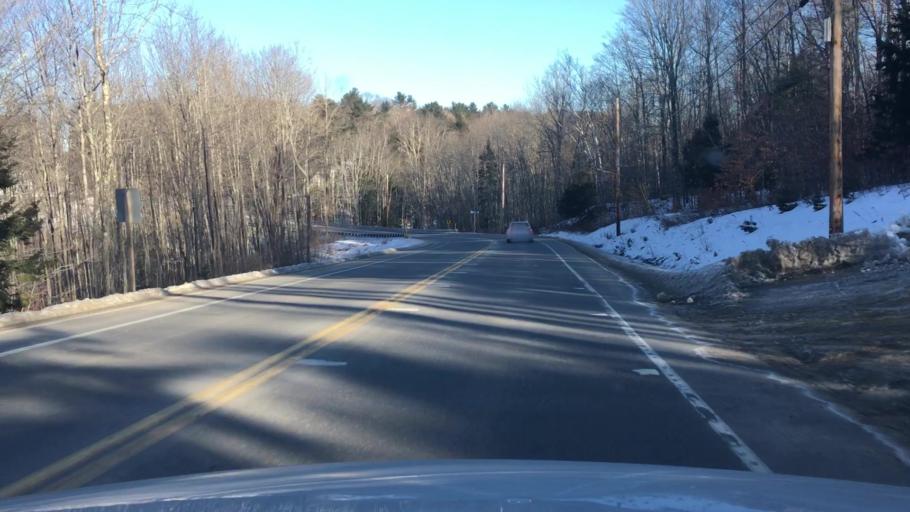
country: US
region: Maine
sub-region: Cumberland County
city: Freeport
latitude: 43.8976
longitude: -70.1140
